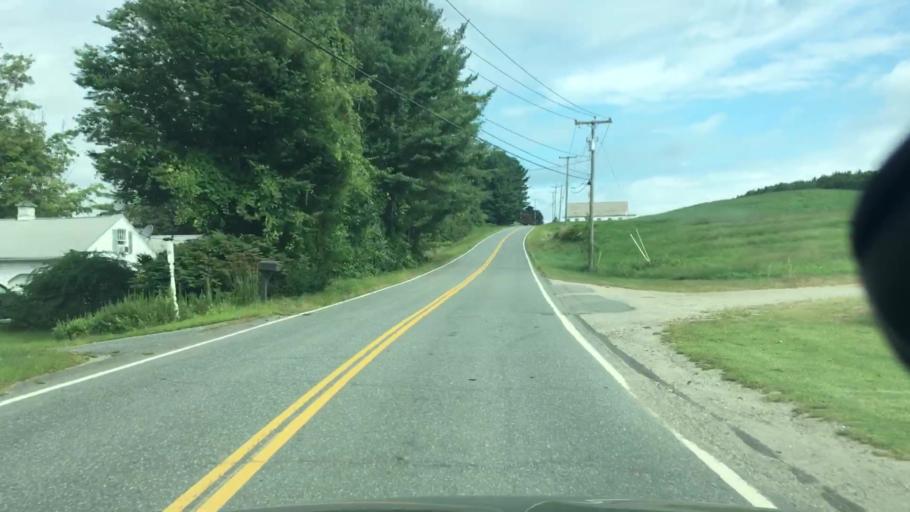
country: US
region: Massachusetts
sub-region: Franklin County
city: Shelburne
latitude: 42.6118
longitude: -72.6725
